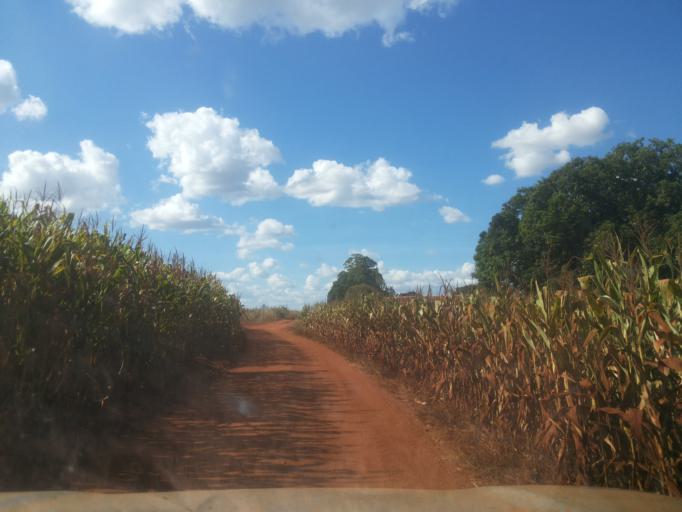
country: BR
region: Minas Gerais
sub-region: Capinopolis
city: Capinopolis
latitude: -18.5812
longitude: -49.4931
